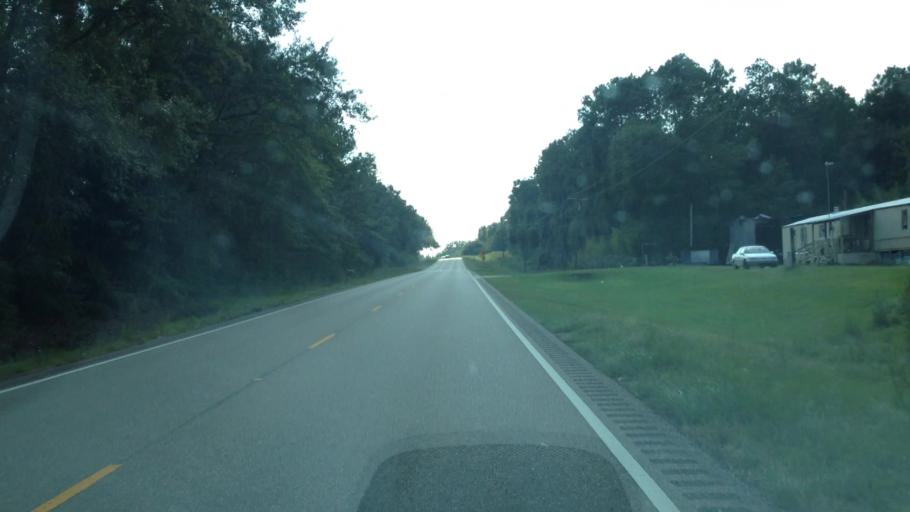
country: US
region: Florida
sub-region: Okaloosa County
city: Crestview
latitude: 31.0355
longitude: -86.6040
